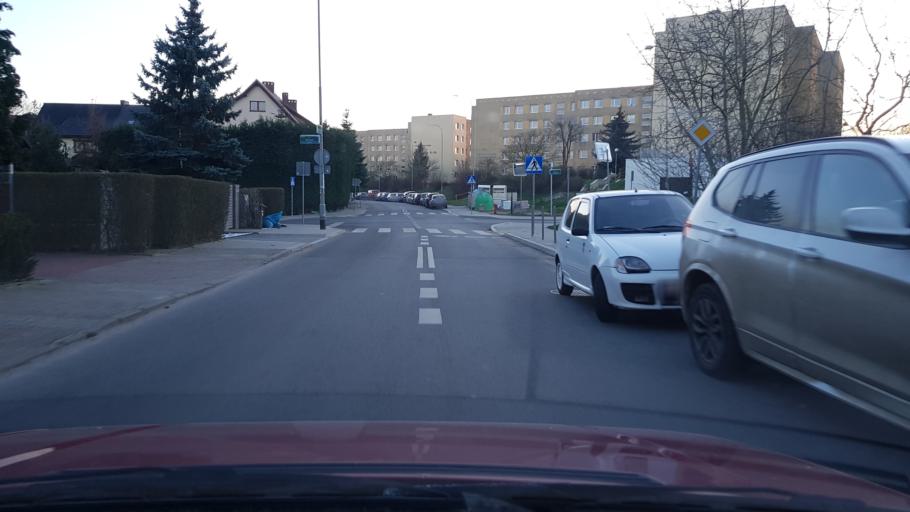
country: PL
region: West Pomeranian Voivodeship
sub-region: Szczecin
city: Szczecin
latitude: 53.4666
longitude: 14.5604
